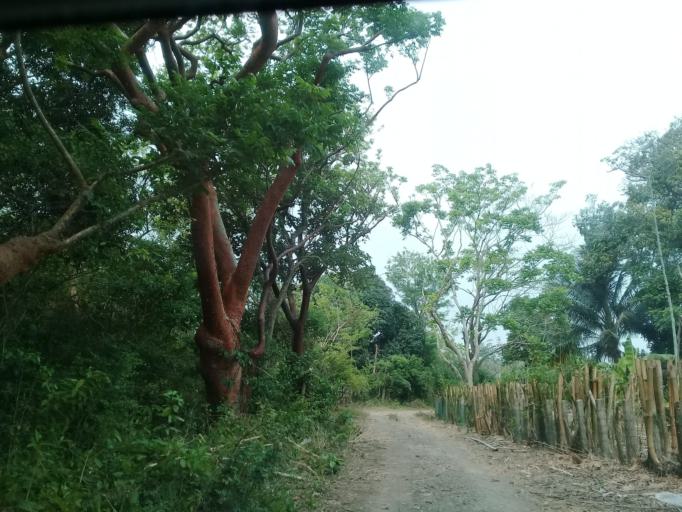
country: MX
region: Veracruz
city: Jamapa
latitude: 19.0502
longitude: -96.1985
